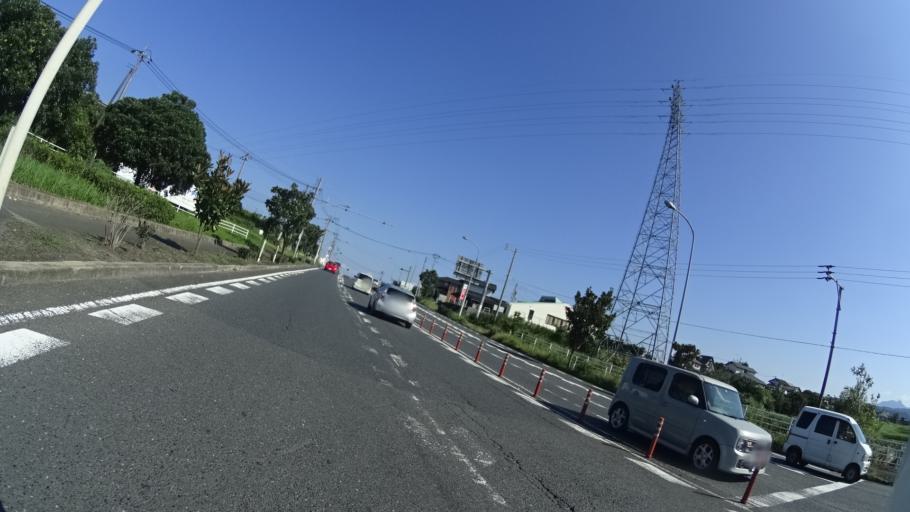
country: JP
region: Fukuoka
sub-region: Buzen-shi
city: Buzen
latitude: 33.6131
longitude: 131.1022
